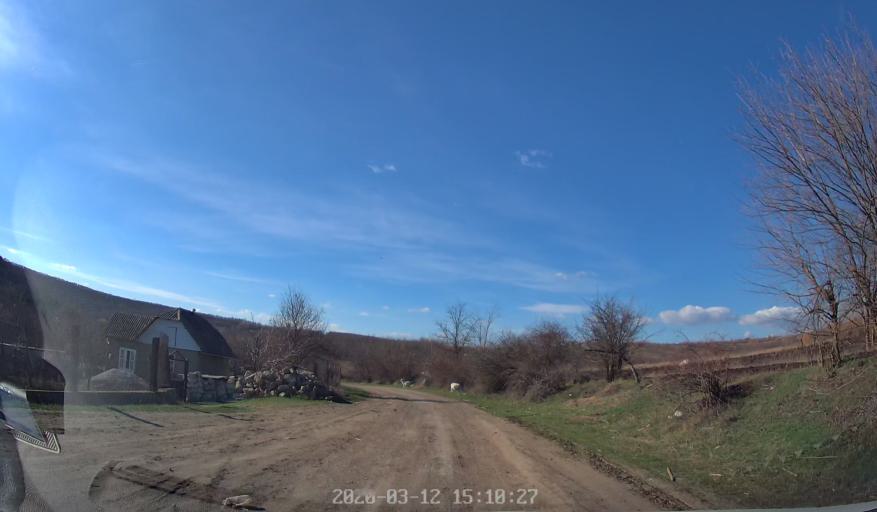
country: MD
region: Chisinau
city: Ciorescu
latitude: 47.2257
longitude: 28.9810
